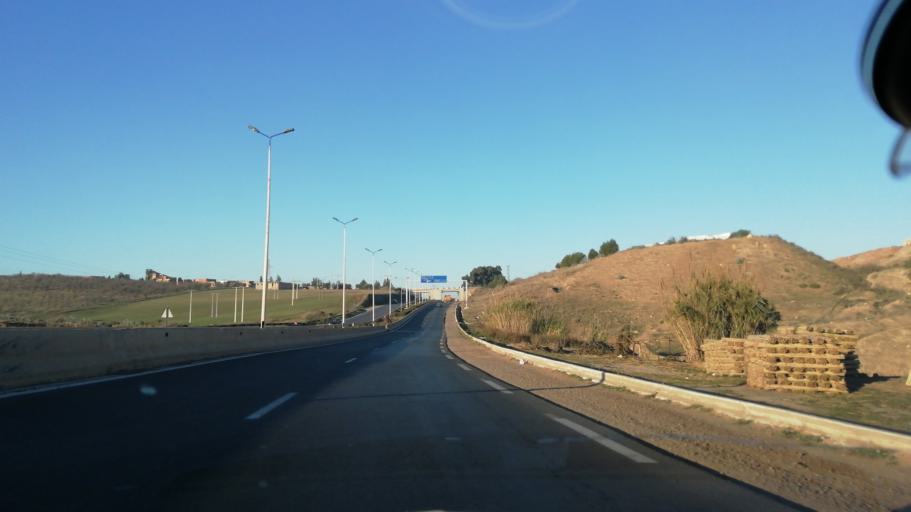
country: DZ
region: Ain Temouchent
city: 'Ain Temouchent
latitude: 35.2962
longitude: -1.1782
